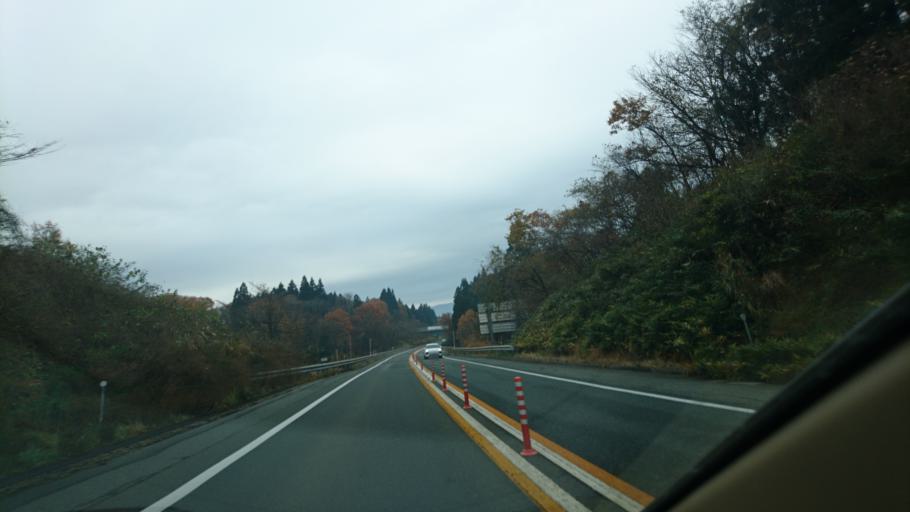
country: JP
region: Iwate
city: Kitakami
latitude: 39.2837
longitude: 140.9986
